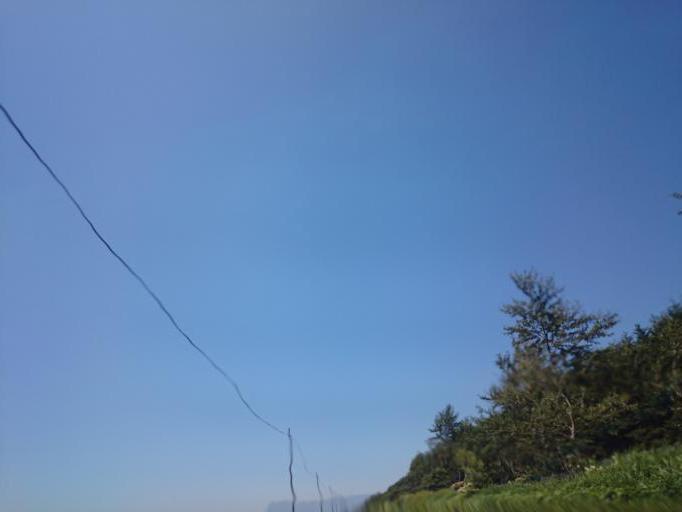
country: JP
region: Hokkaido
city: Ebetsu
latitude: 43.0741
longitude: 141.5787
